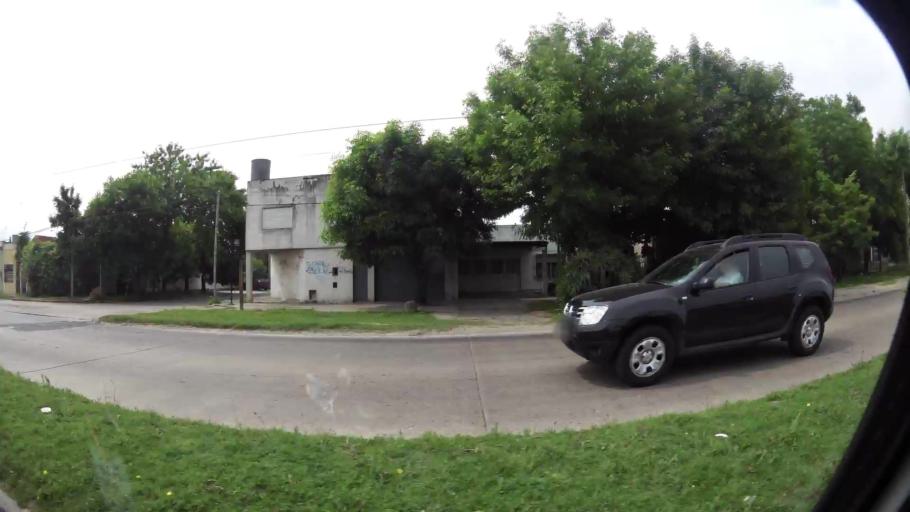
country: AR
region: Buenos Aires
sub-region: Partido de La Plata
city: La Plata
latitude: -34.8985
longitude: -57.9916
